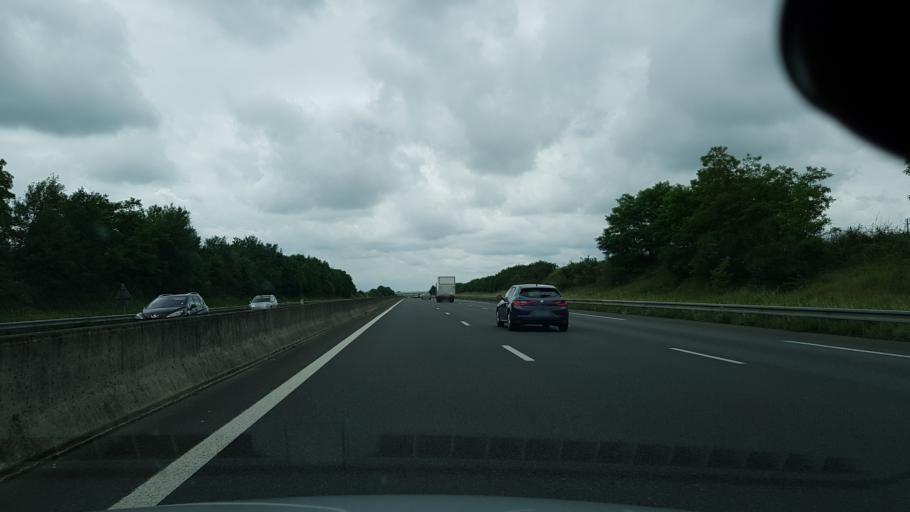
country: FR
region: Centre
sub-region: Departement du Loir-et-Cher
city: Herbault
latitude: 47.5748
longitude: 1.0569
